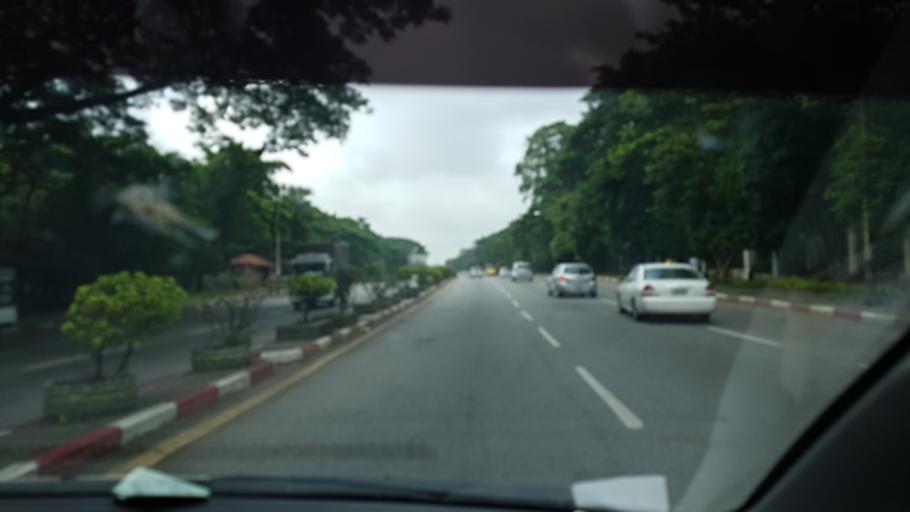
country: MM
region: Yangon
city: Yangon
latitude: 16.7990
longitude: 96.1386
